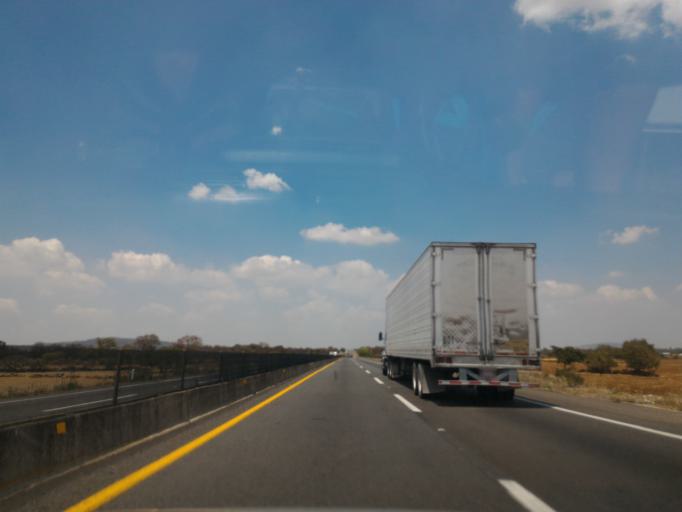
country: MX
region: Jalisco
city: Tepatitlan de Morelos
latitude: 20.8607
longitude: -102.7641
